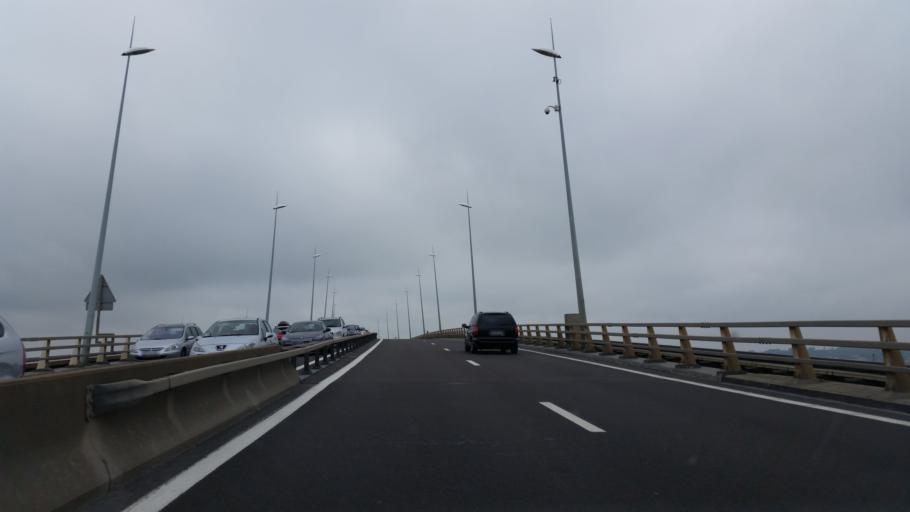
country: FR
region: Haute-Normandie
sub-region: Departement de la Seine-Maritime
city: Rogerville
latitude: 49.4631
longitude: 0.2745
